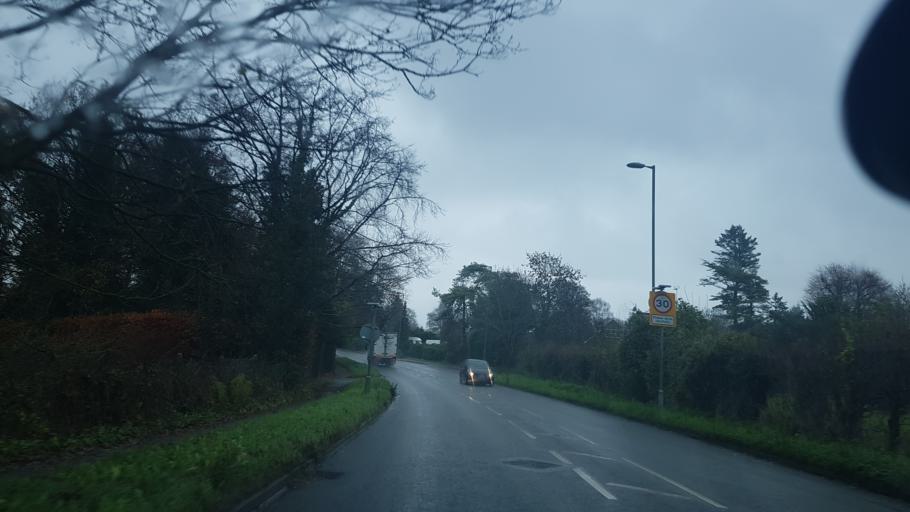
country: GB
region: England
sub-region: Surrey
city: Great Bookham
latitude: 51.2733
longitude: -0.3796
